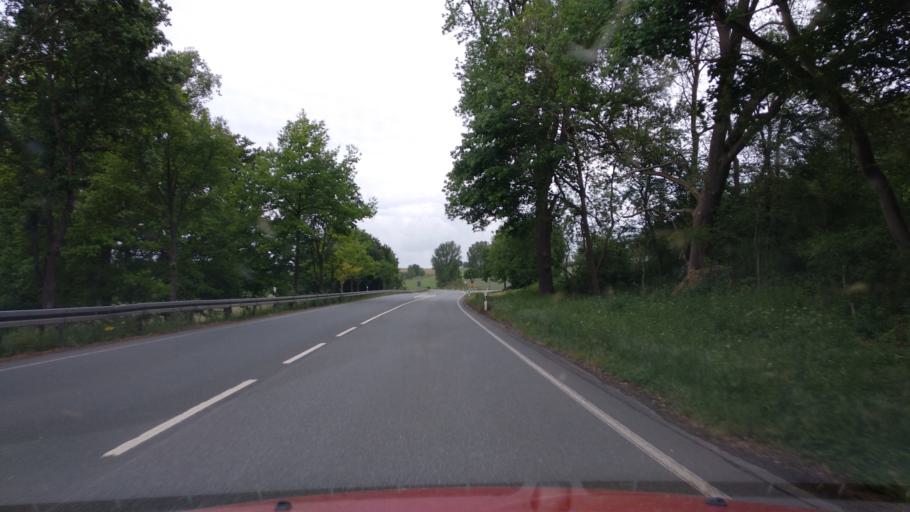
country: DE
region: North Rhine-Westphalia
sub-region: Regierungsbezirk Detmold
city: Willebadessen
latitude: 51.6283
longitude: 9.0818
